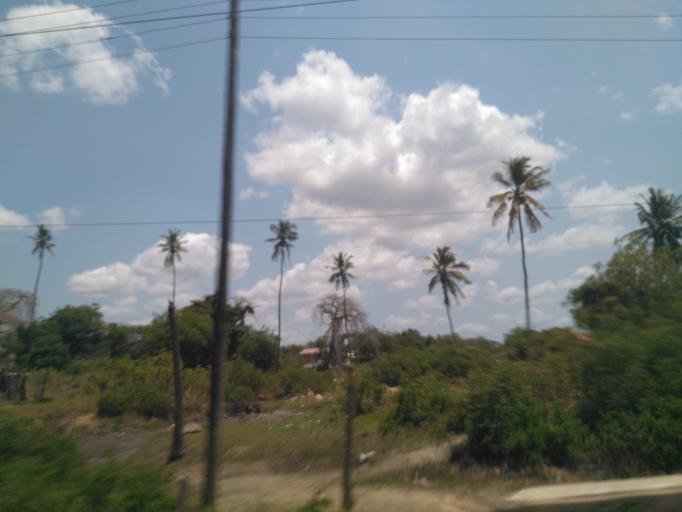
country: TZ
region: Dar es Salaam
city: Dar es Salaam
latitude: -6.8308
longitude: 39.3390
